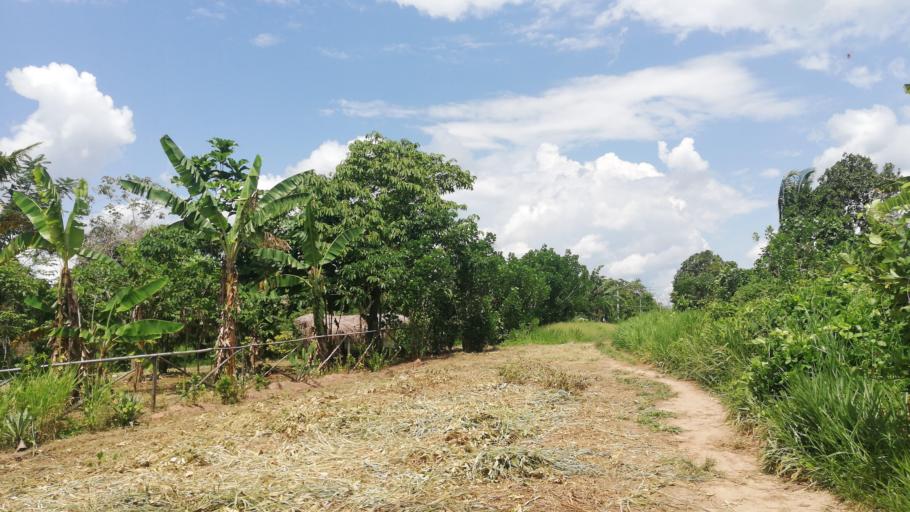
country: PE
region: Ucayali
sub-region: Provincia de Coronel Portillo
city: Puerto Callao
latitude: -8.2701
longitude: -74.6510
